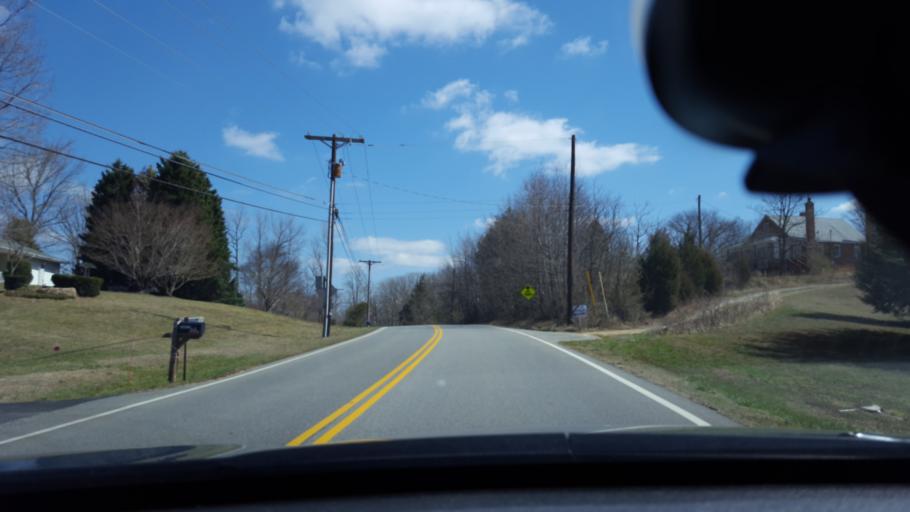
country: US
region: Maryland
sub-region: Calvert County
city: Huntingtown
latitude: 38.6269
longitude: -76.5955
